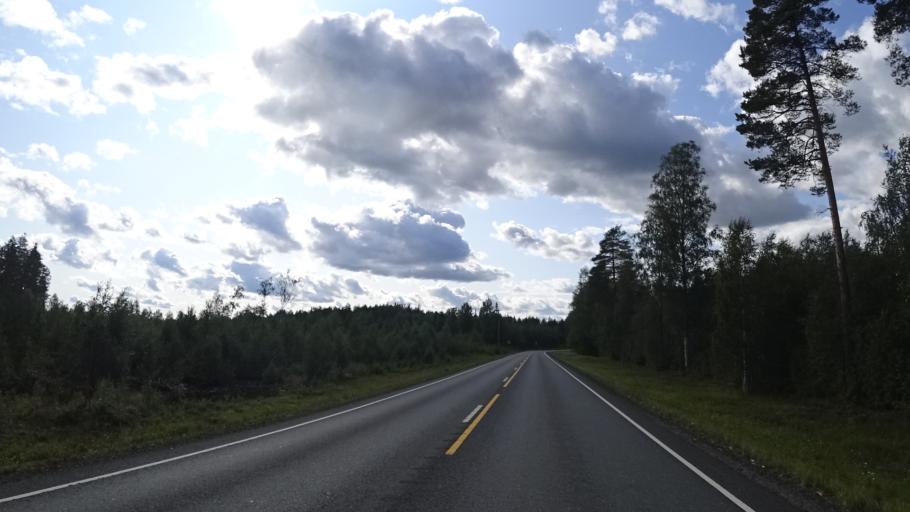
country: RU
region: Republic of Karelia
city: Vyartsilya
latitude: 62.1755
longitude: 30.5549
